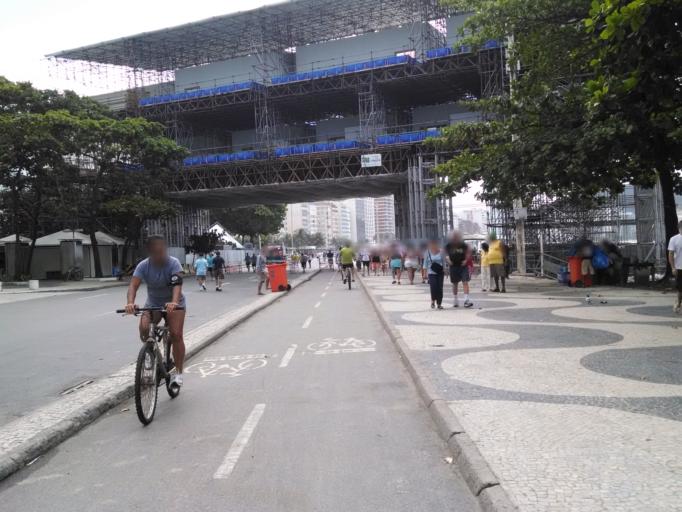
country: BR
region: Rio de Janeiro
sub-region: Rio De Janeiro
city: Rio de Janeiro
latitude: -22.9860
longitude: -43.1888
